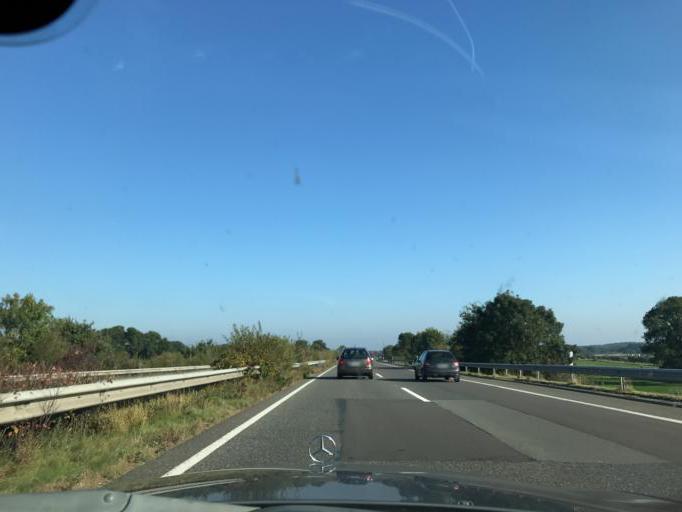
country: DE
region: Lower Saxony
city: Leer
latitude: 53.2660
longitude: 7.4700
